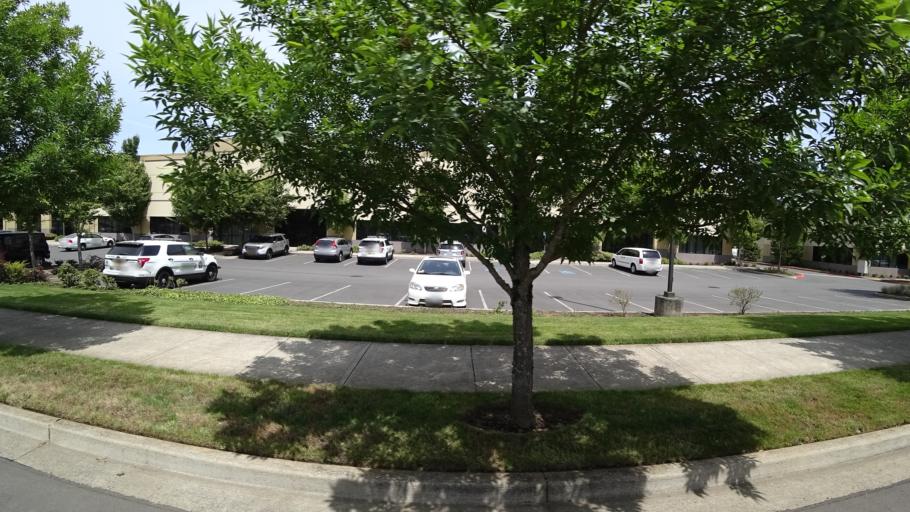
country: US
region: Oregon
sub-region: Multnomah County
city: Fairview
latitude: 45.5452
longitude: -122.4881
